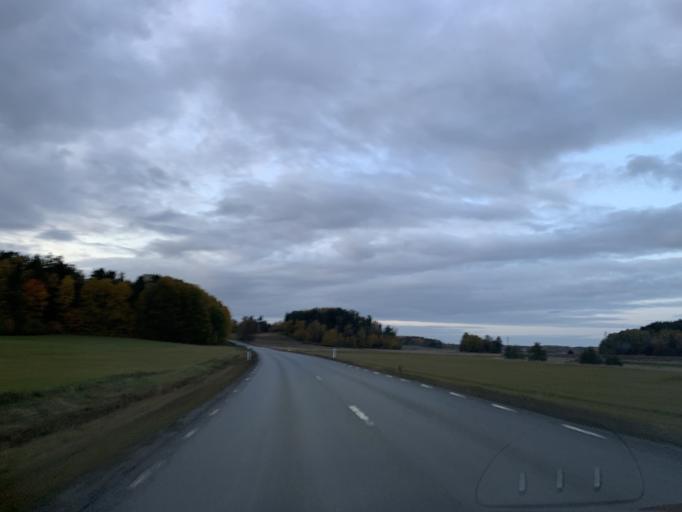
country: SE
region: Stockholm
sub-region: Nynashamns Kommun
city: Osmo
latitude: 59.0138
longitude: 17.8055
